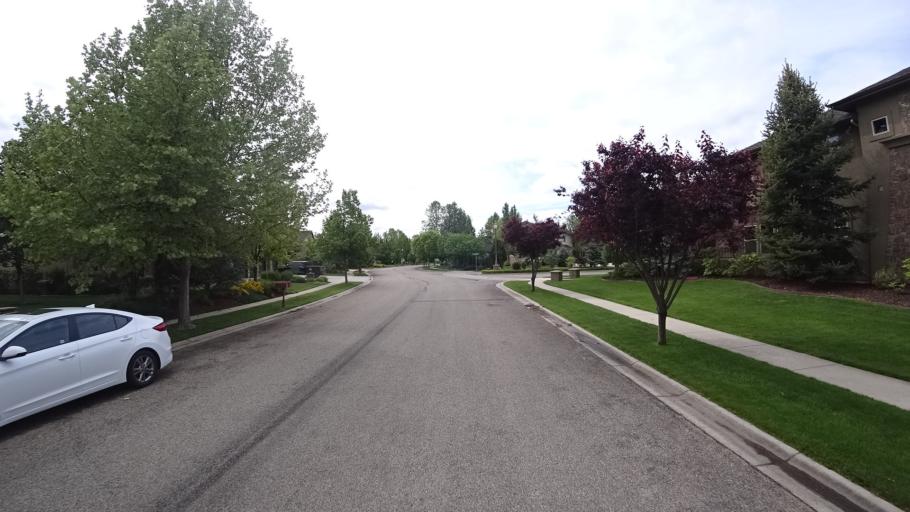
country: US
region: Idaho
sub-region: Ada County
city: Eagle
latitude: 43.6806
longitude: -116.3627
